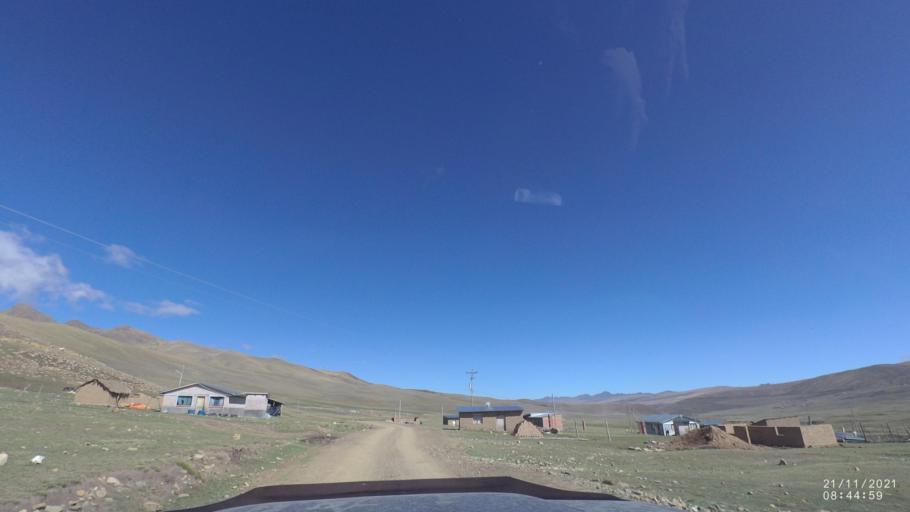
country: BO
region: Cochabamba
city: Cochabamba
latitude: -17.2507
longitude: -66.2295
